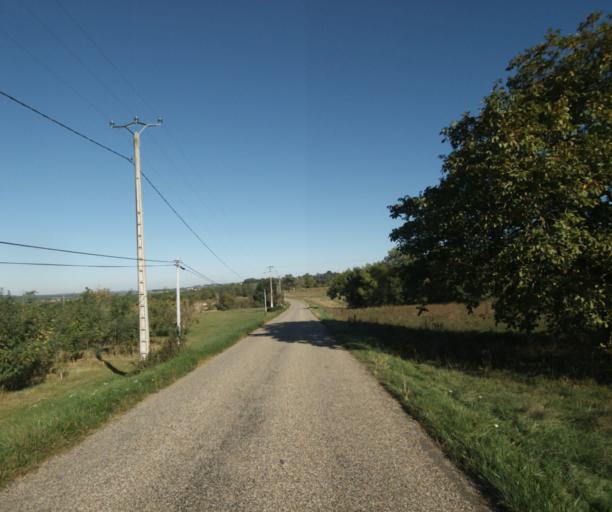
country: FR
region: Midi-Pyrenees
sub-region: Departement du Gers
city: Gondrin
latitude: 43.8326
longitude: 0.2555
